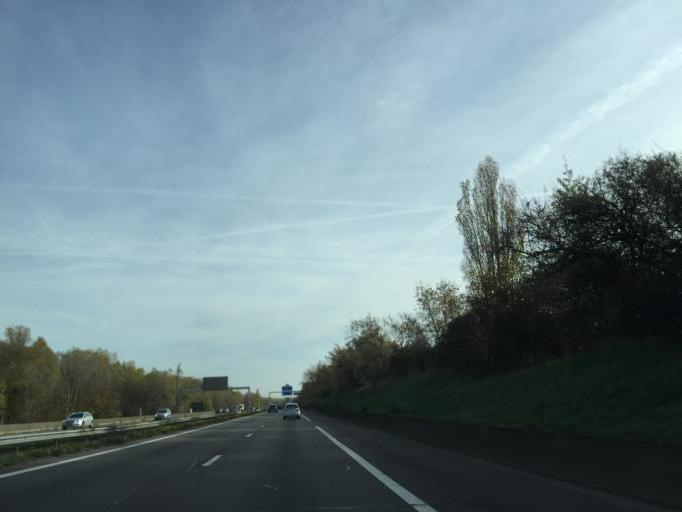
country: FR
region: Rhone-Alpes
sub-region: Departement du Rhone
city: Vaulx-en-Velin
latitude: 45.7920
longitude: 4.9143
